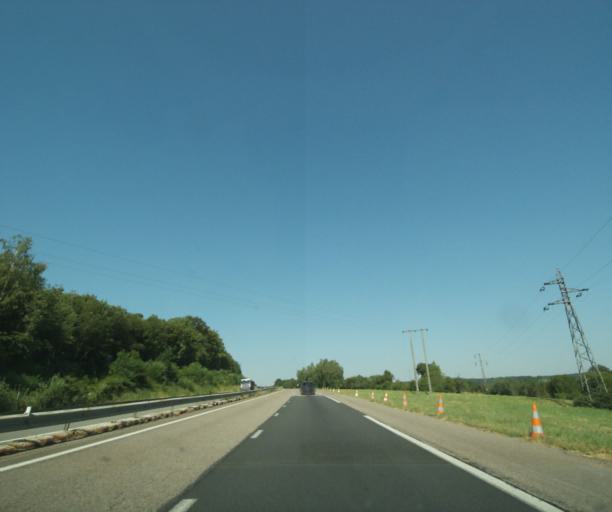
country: FR
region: Lorraine
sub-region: Departement de Meurthe-et-Moselle
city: Foug
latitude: 48.6702
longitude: 5.8025
